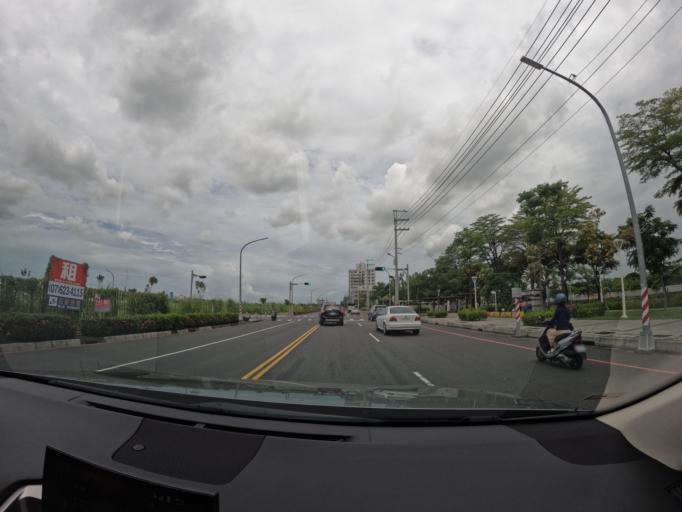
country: TW
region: Kaohsiung
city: Kaohsiung
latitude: 22.7846
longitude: 120.2953
